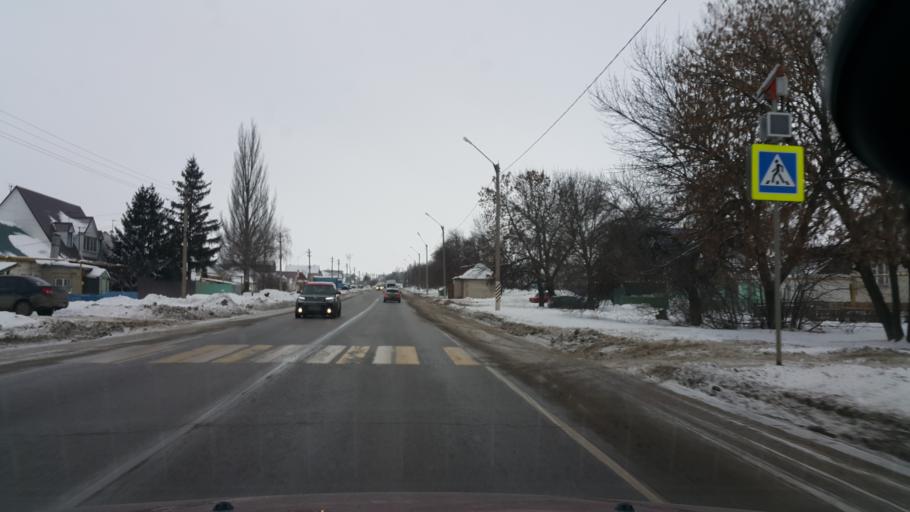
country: RU
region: Tambov
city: Pokrovo-Prigorodnoye
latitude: 52.6878
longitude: 41.4328
